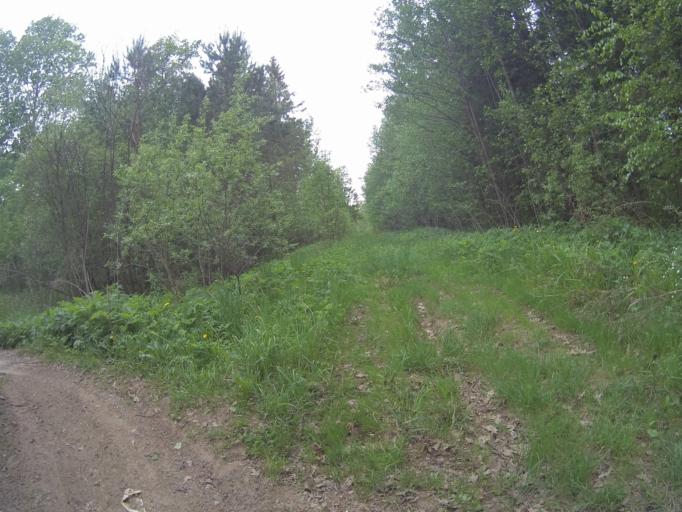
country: RU
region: Vladimir
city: Golovino
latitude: 56.0003
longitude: 40.4189
